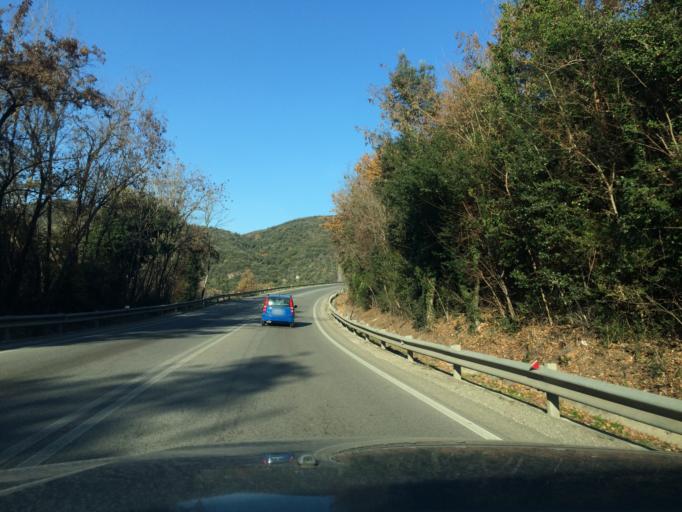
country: IT
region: Umbria
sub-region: Provincia di Terni
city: Fornole
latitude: 42.5347
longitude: 12.4754
